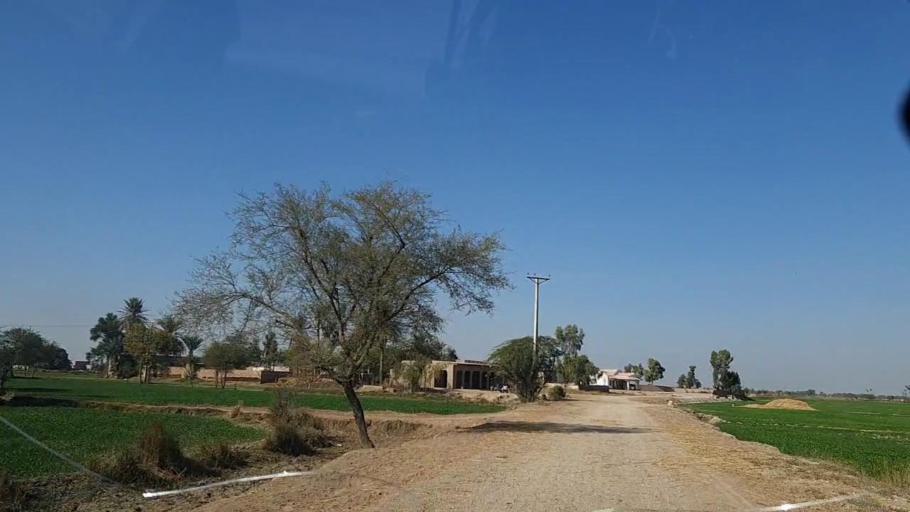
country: PK
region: Sindh
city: Khanpur
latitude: 27.8489
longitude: 69.3924
